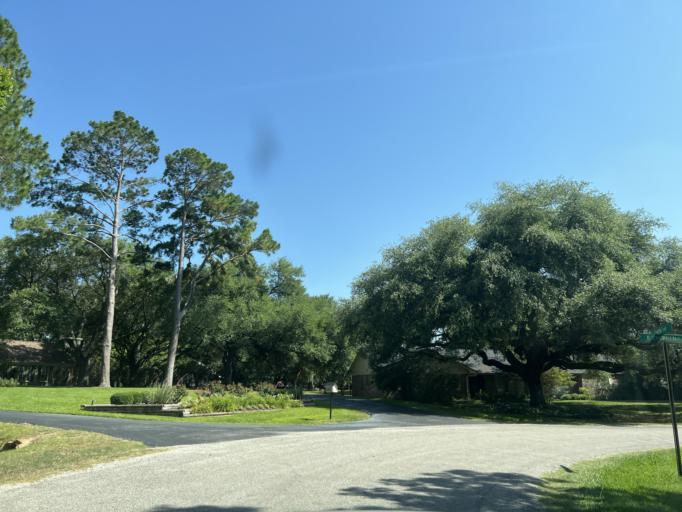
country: US
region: Texas
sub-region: Washington County
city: Brenham
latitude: 30.1502
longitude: -96.3605
